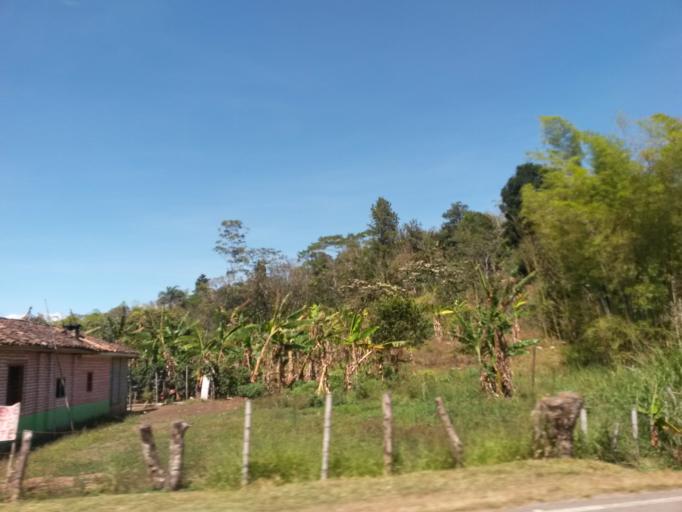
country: CO
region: Cauca
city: Lopez
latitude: 2.4411
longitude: -76.7789
